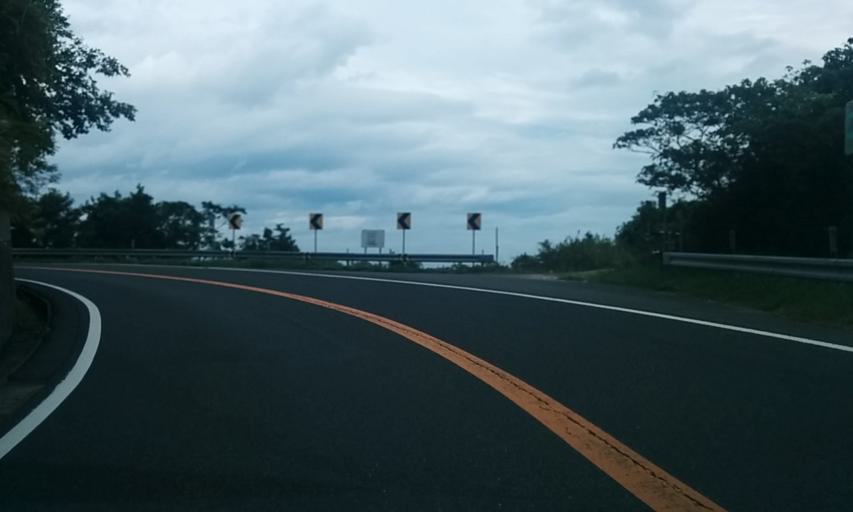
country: JP
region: Kyoto
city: Miyazu
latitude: 35.5320
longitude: 135.2693
